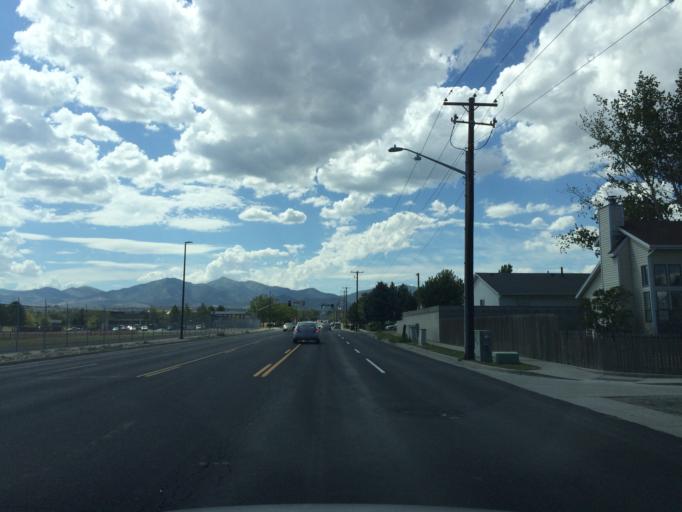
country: US
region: Utah
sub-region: Salt Lake County
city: Kearns
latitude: 40.6386
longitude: -111.9976
